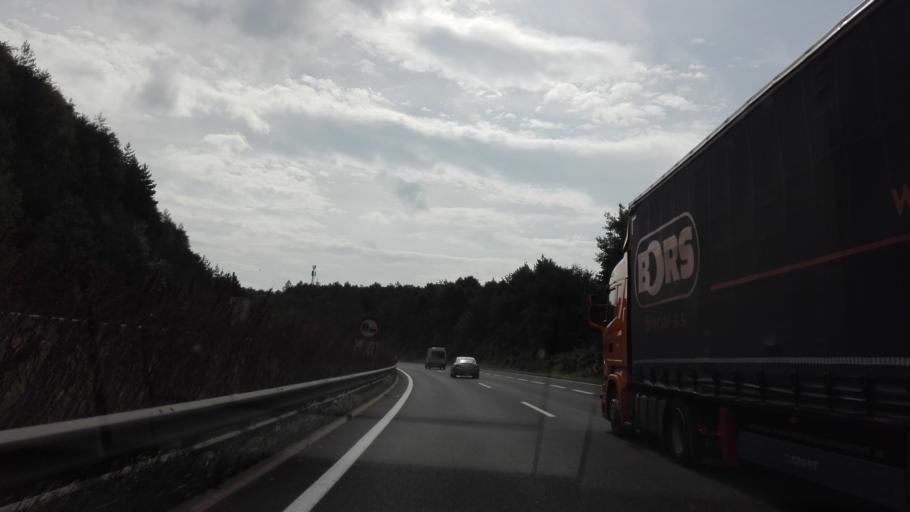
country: AT
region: Lower Austria
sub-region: Politischer Bezirk Baden
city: Alland
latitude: 48.0572
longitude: 16.0998
